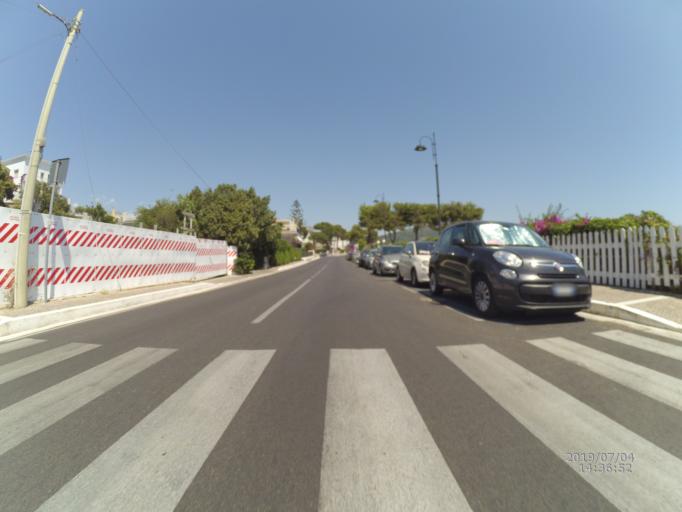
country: IT
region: Latium
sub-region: Provincia di Latina
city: Gaeta
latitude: 41.2119
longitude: 13.5565
